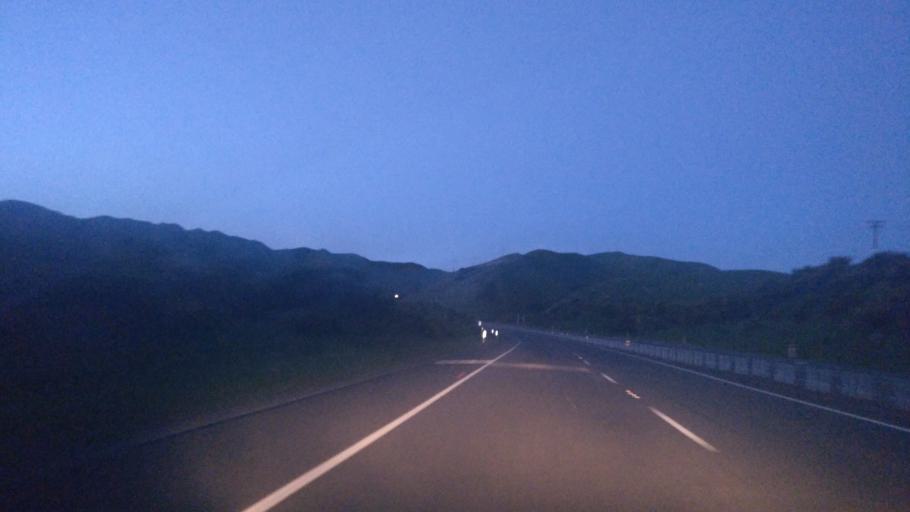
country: NZ
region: Wellington
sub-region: Porirua City
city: Porirua
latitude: -41.0661
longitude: 174.8771
